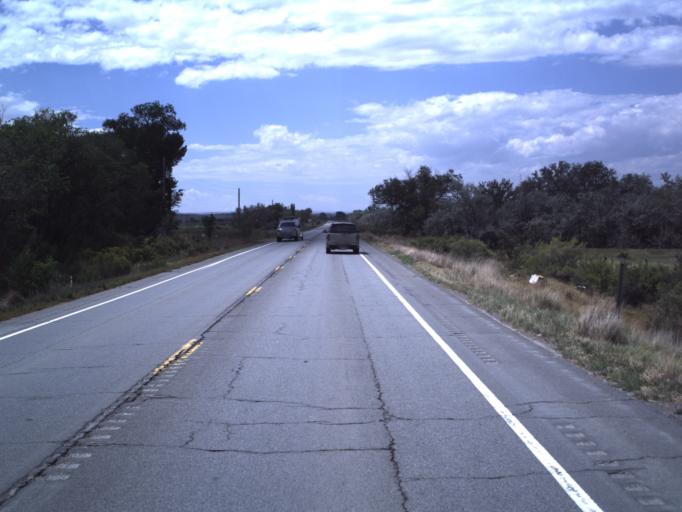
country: US
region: Utah
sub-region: Duchesne County
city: Duchesne
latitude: 40.1572
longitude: -110.1842
